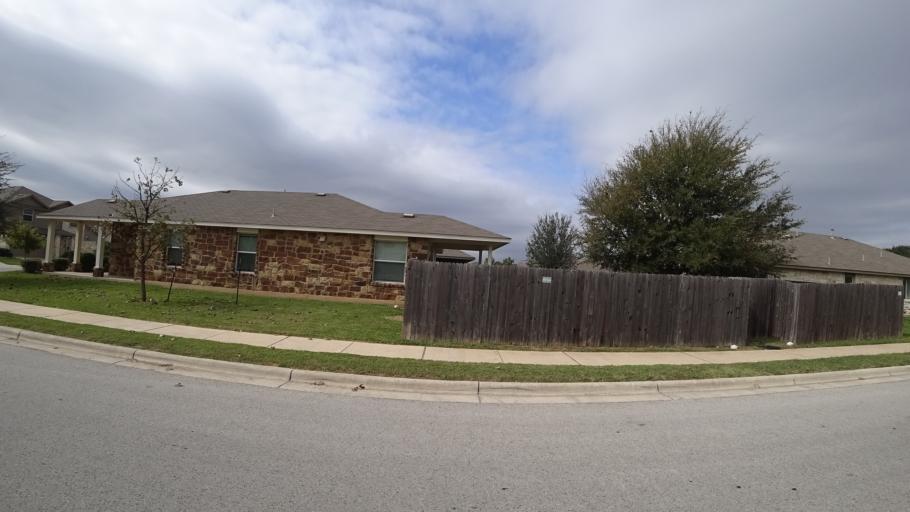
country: US
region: Texas
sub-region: Travis County
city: Shady Hollow
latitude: 30.1546
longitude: -97.8473
